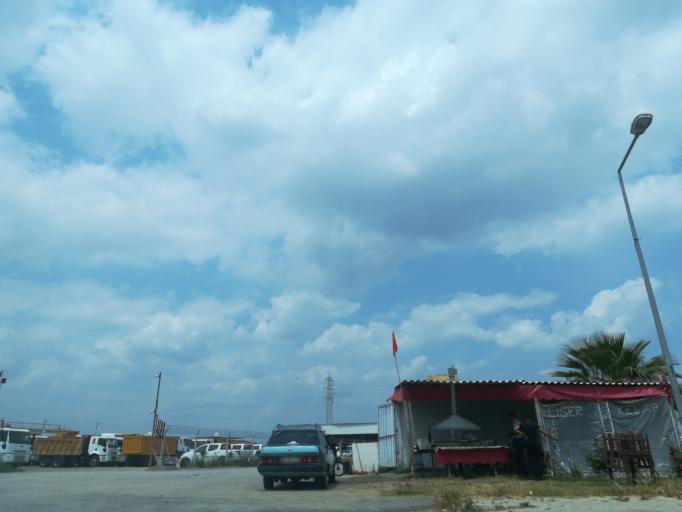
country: TR
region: Adana
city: Seyhan
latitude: 37.0043
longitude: 35.2489
